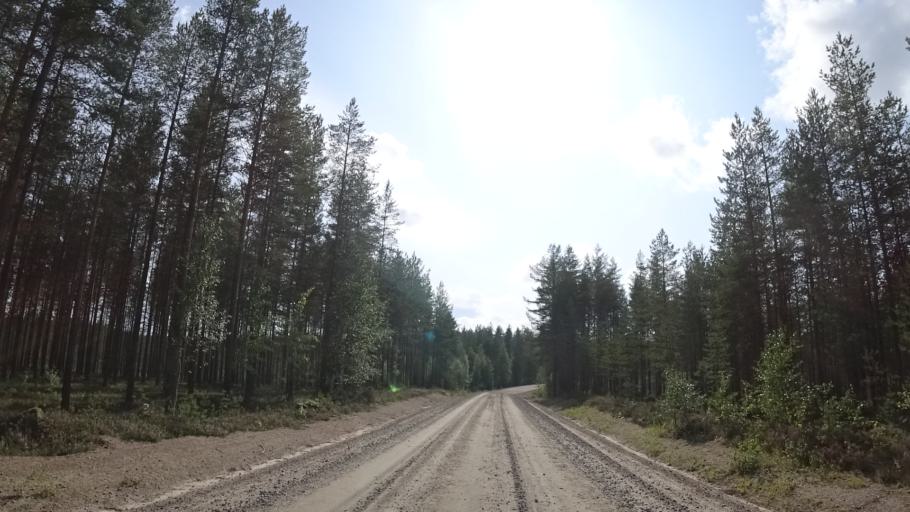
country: FI
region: North Karelia
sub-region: Pielisen Karjala
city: Lieksa
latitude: 63.5426
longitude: 30.0523
